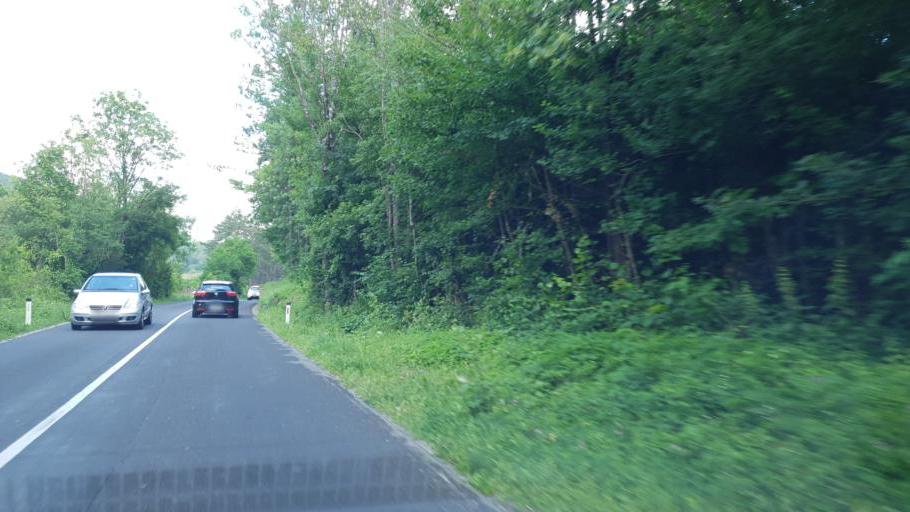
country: SI
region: Ilirska Bistrica
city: Ilirska Bistrica
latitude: 45.5848
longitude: 14.2347
